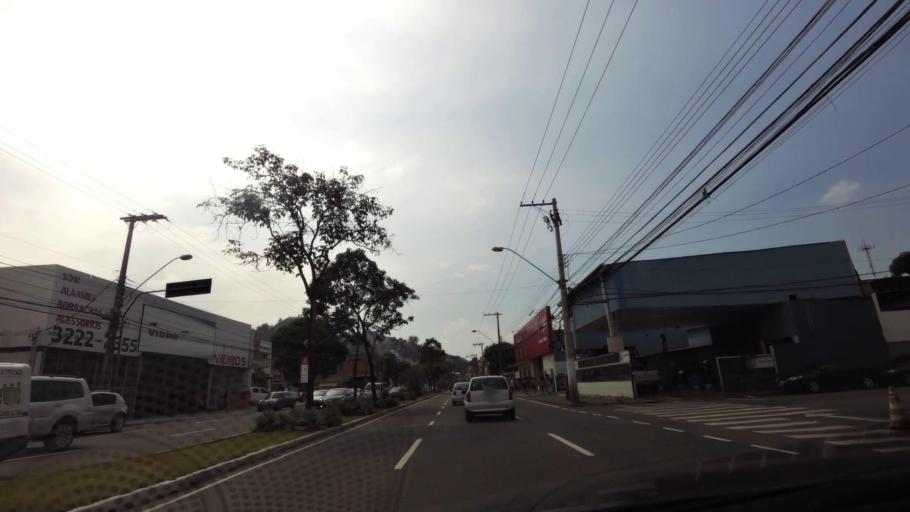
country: BR
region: Espirito Santo
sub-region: Vitoria
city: Vitoria
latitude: -20.3108
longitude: -40.3141
